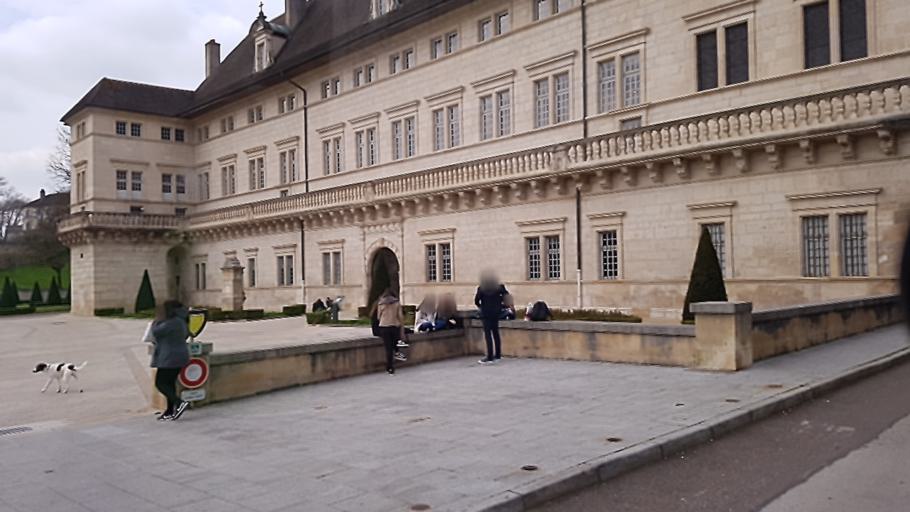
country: FR
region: Franche-Comte
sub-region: Departement du Jura
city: Dole
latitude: 47.0901
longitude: 5.4935
